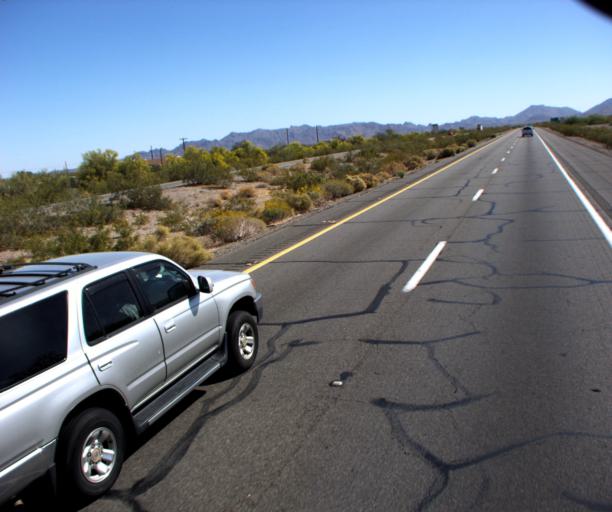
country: US
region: Arizona
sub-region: La Paz County
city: Quartzsite
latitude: 33.6667
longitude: -114.1882
